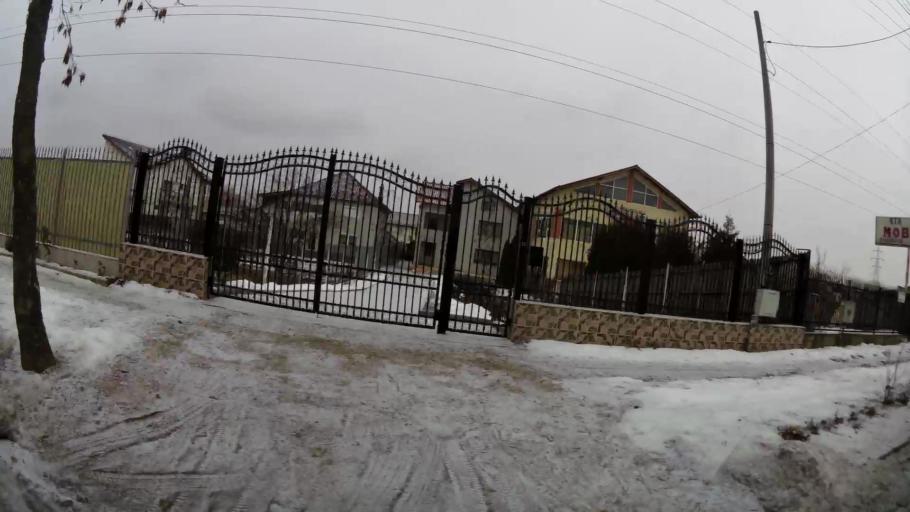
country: RO
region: Dambovita
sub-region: Municipiul Targoviste
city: Targoviste
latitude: 44.9307
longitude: 25.4760
